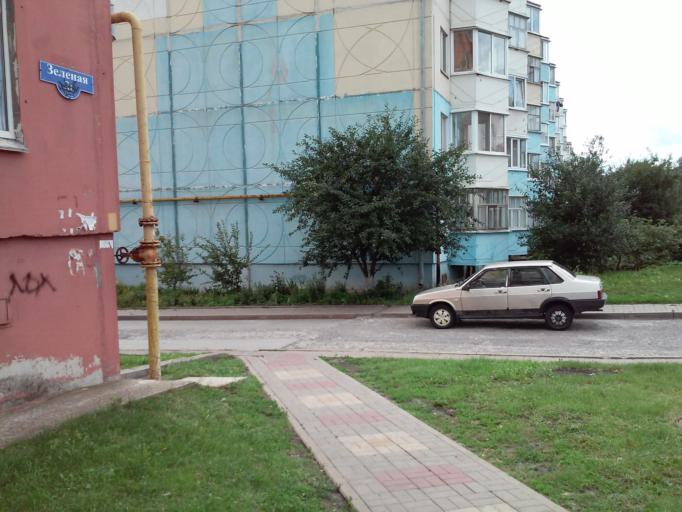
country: RU
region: Belgorod
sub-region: Belgorodskiy Rayon
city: Belgorod
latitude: 50.5377
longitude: 36.5775
